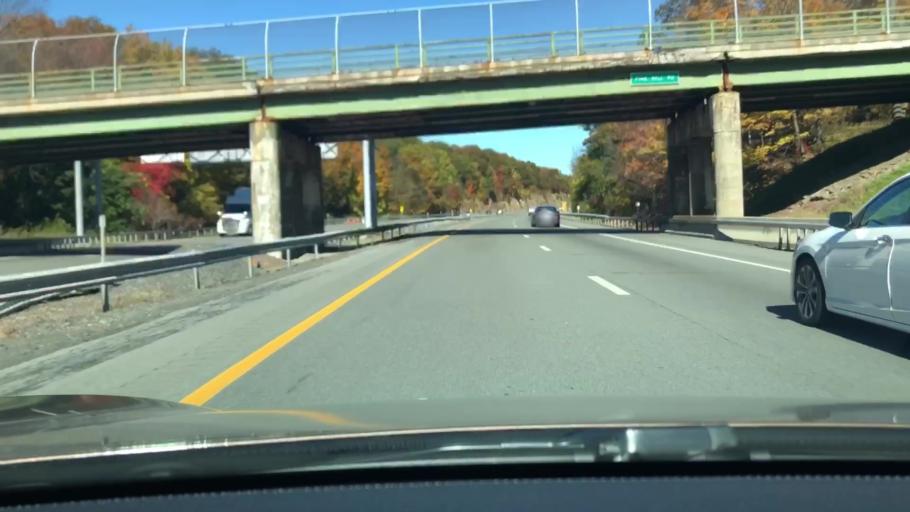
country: US
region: New York
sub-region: Orange County
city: Highland Mills
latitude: 41.3425
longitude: -74.1172
